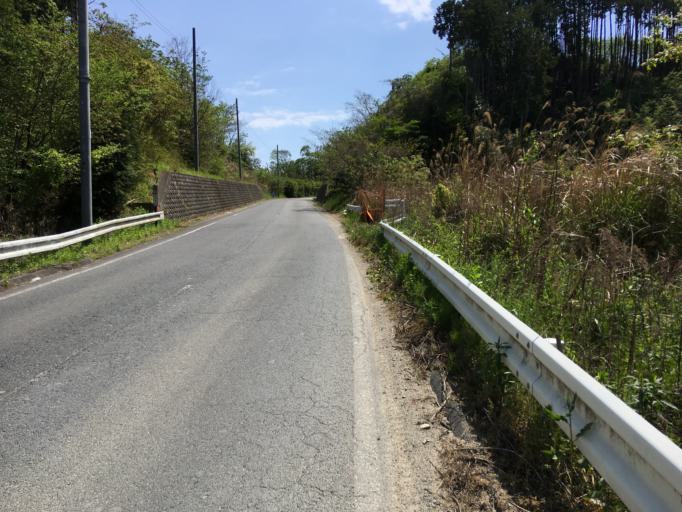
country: JP
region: Nara
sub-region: Ikoma-shi
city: Ikoma
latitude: 34.6448
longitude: 135.6831
